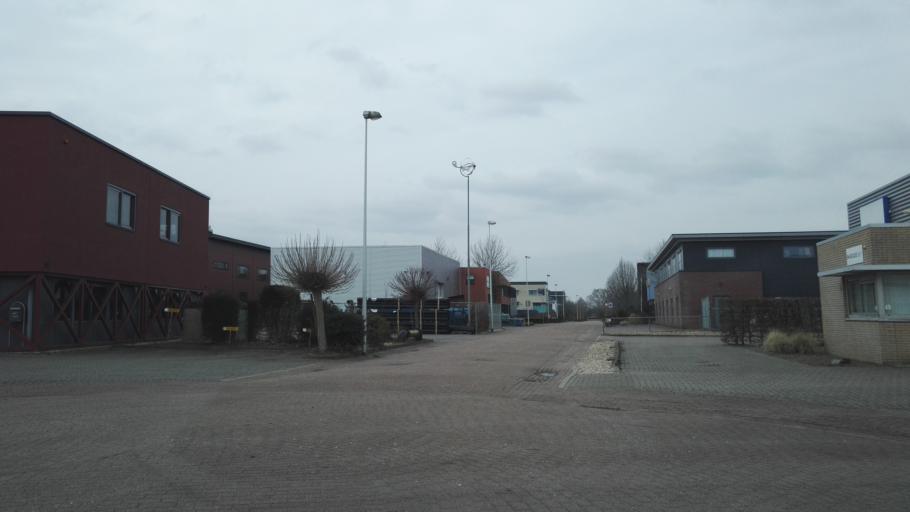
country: NL
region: Gelderland
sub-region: Gemeente Apeldoorn
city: Apeldoorn
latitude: 52.2413
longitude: 5.9877
